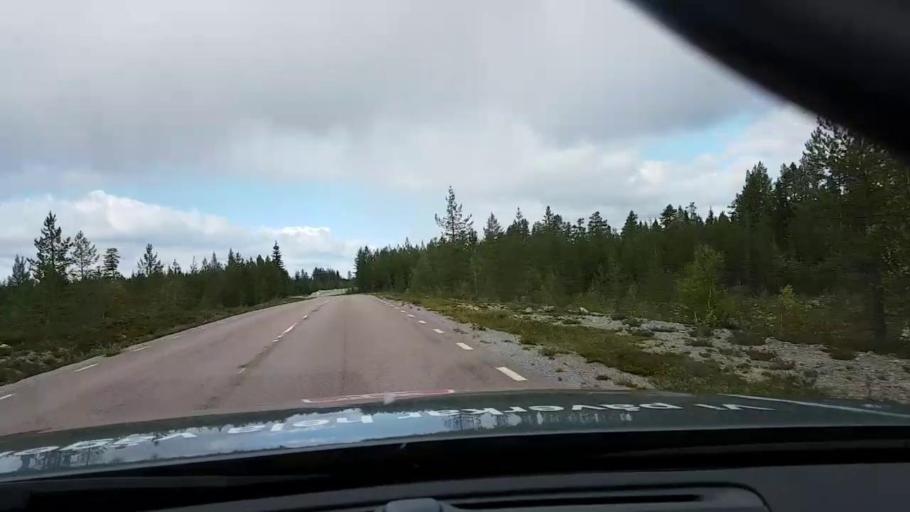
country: SE
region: Vaesterbotten
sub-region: Asele Kommun
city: Asele
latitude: 63.8846
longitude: 17.3529
